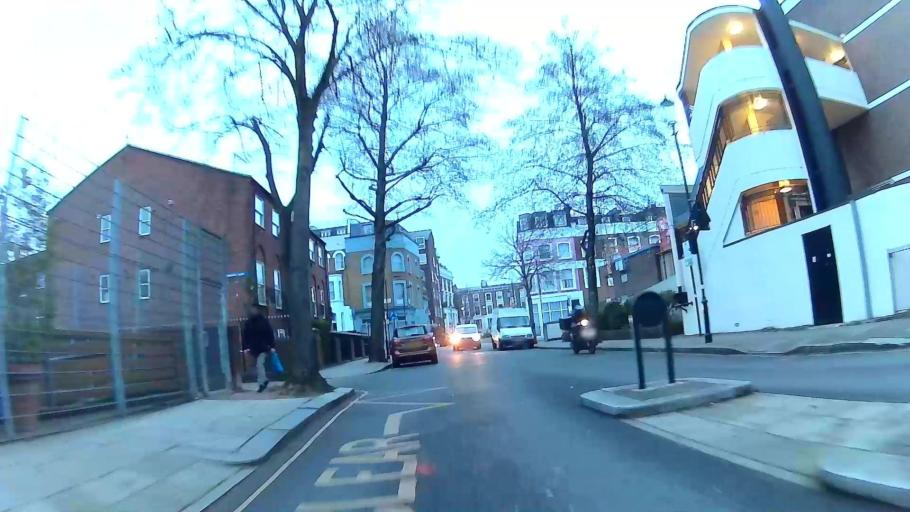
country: GB
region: England
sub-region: Greater London
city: Kensington
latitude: 51.5153
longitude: -0.2113
